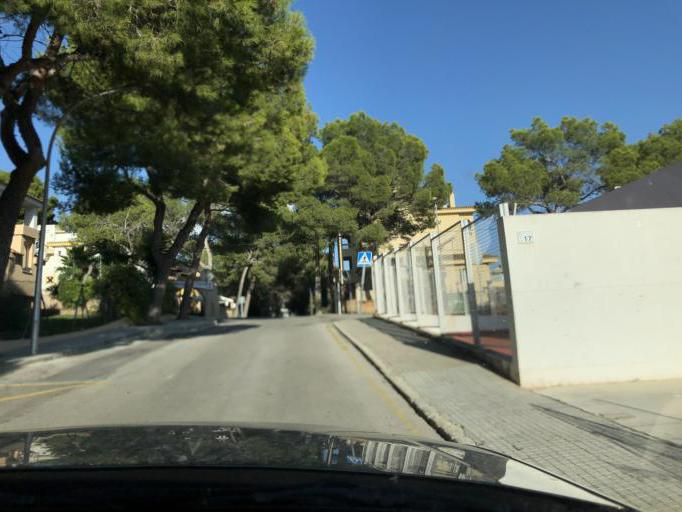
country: ES
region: Balearic Islands
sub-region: Illes Balears
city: Camp de Mar
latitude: 39.5392
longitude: 2.4482
